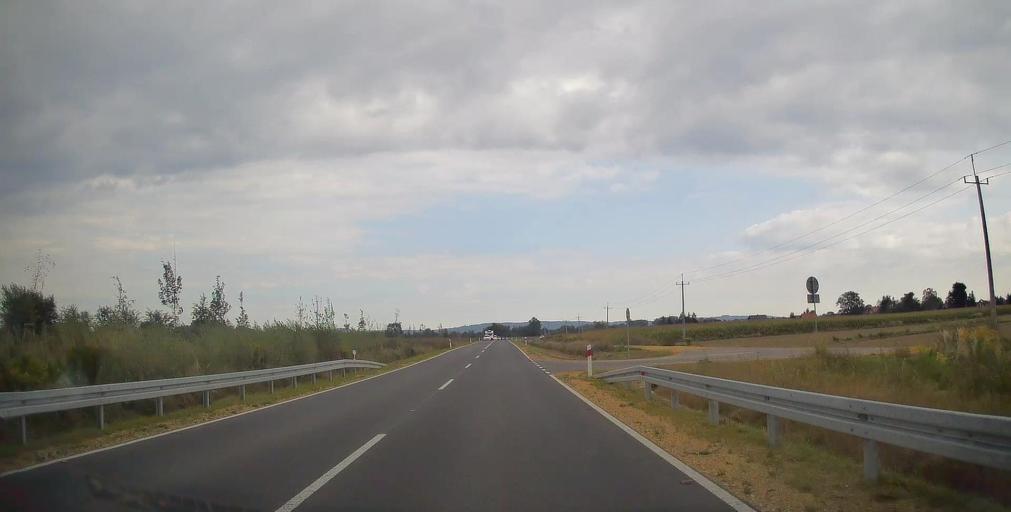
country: PL
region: Lesser Poland Voivodeship
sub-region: Powiat oswiecimski
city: Zator
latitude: 50.0154
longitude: 19.4272
